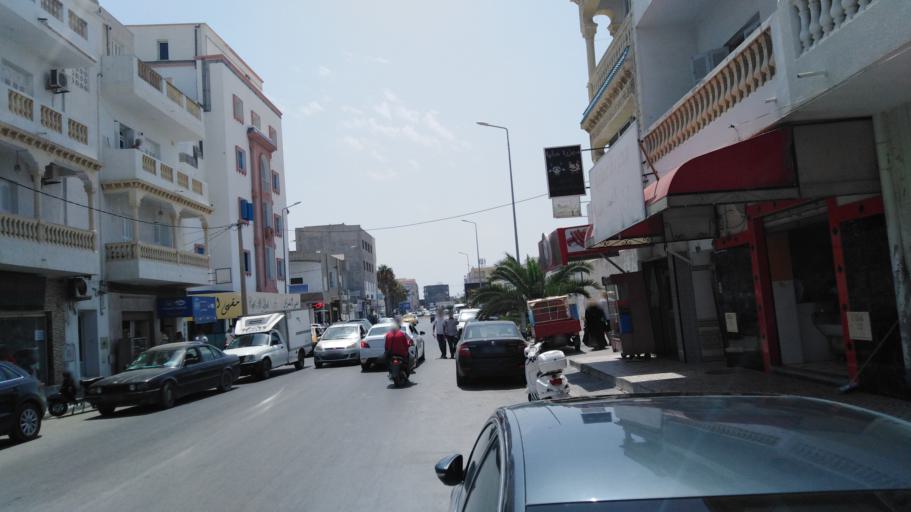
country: TN
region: Al Mahdiyah
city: Mahdia
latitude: 35.5095
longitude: 11.0514
